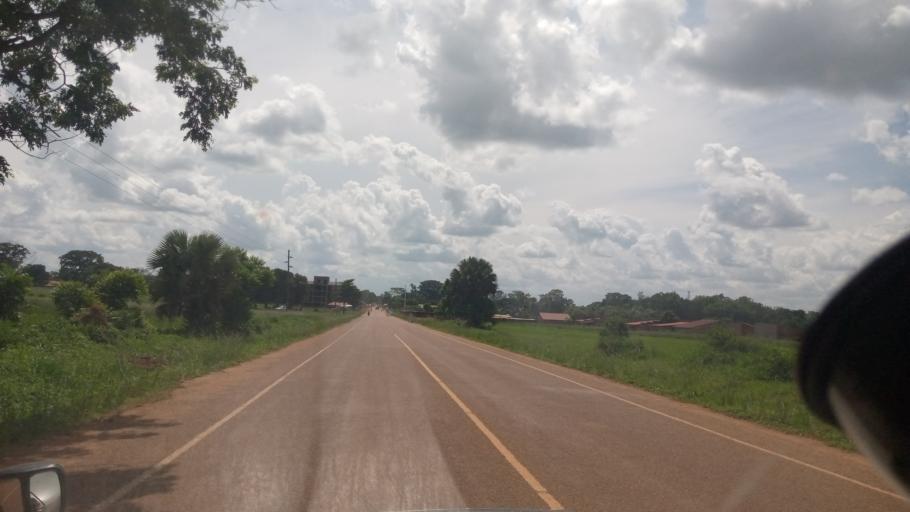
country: UG
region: Northern Region
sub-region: Lira District
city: Lira
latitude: 2.2471
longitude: 32.9071
